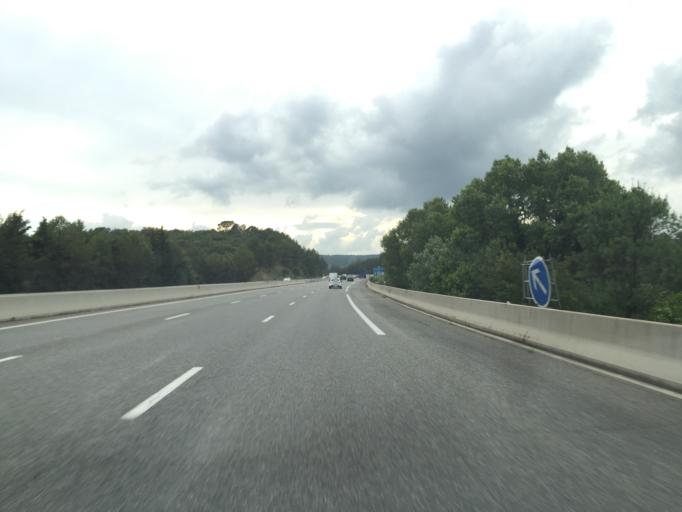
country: FR
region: Provence-Alpes-Cote d'Azur
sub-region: Departement du Var
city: Cabasse
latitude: 43.4016
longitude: 6.2171
